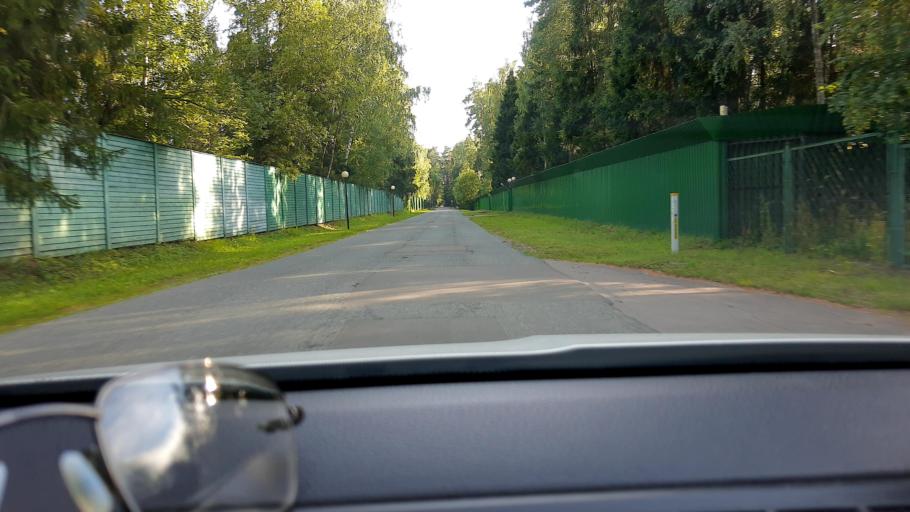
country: RU
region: Moskovskaya
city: Nikolina Gora
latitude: 55.7214
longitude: 36.9627
